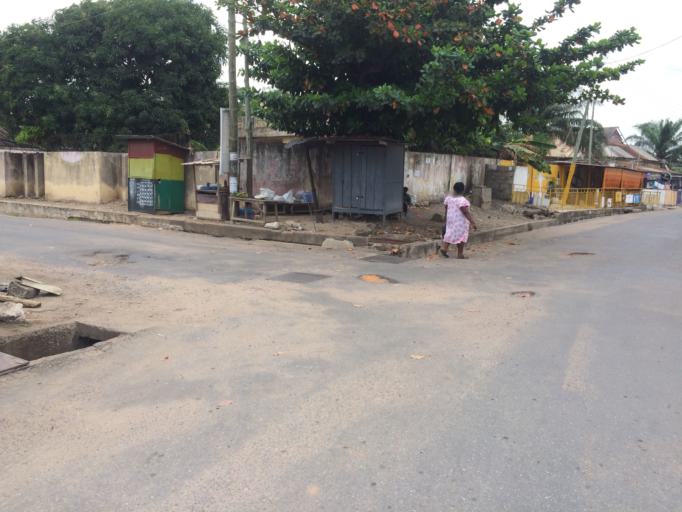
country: GH
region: Greater Accra
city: Accra
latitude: 5.5560
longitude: -0.1808
